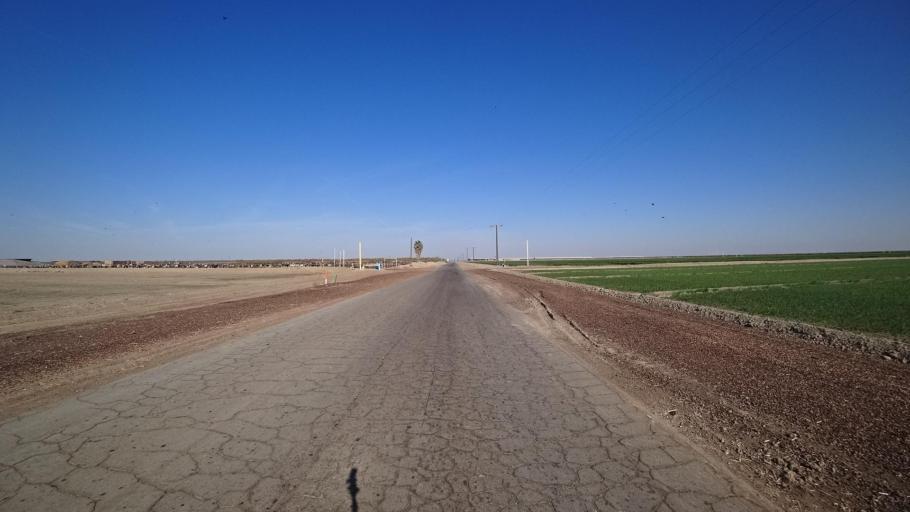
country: US
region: California
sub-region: Kern County
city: Wasco
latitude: 35.7242
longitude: -119.4193
